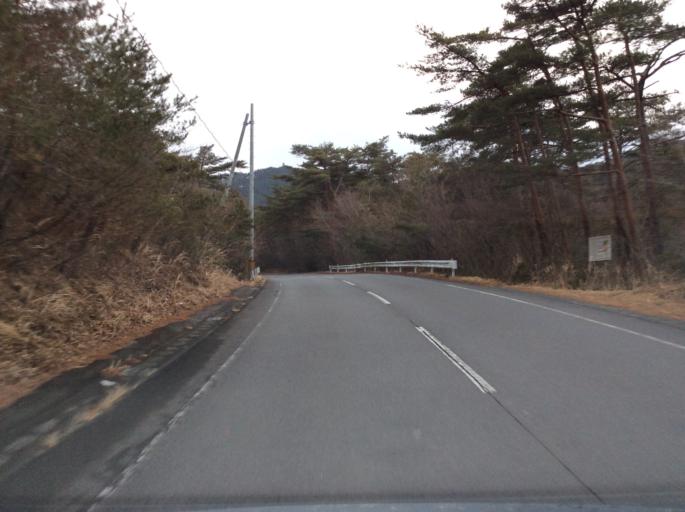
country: JP
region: Fukushima
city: Iwaki
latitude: 37.1486
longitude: 140.9385
